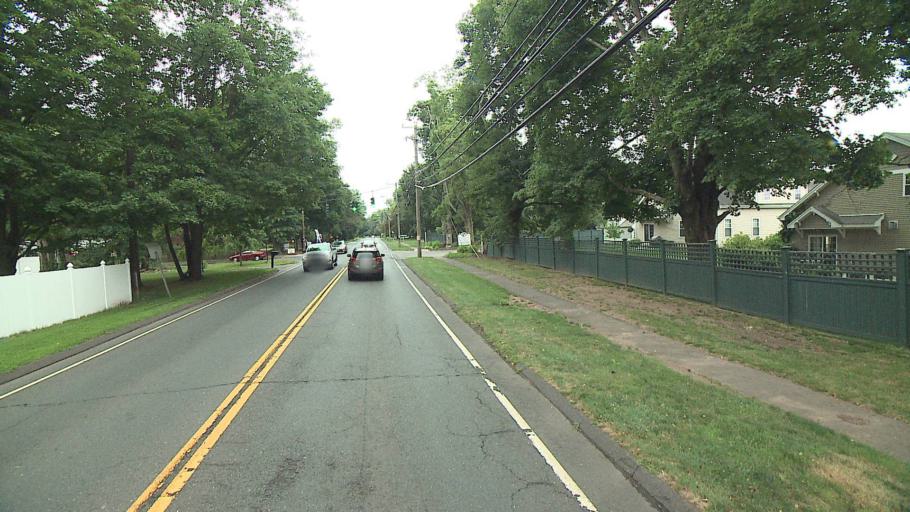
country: US
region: Connecticut
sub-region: Middlesex County
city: Middletown
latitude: 41.5697
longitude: -72.6713
